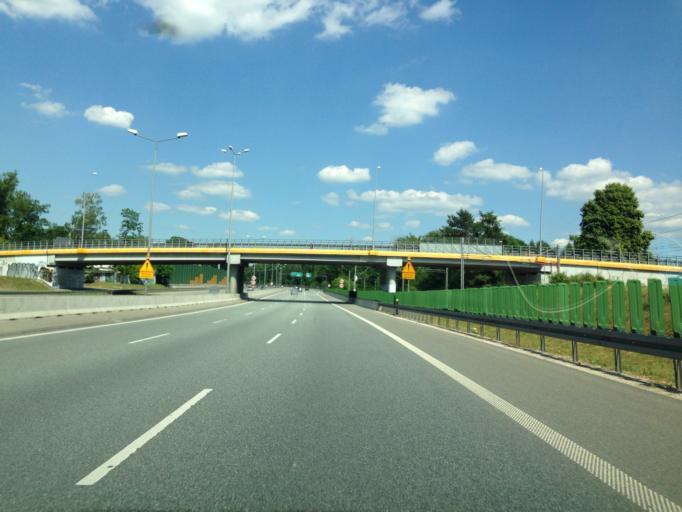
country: PL
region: Masovian Voivodeship
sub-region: Warszawa
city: Bemowo
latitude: 52.2495
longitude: 20.9375
